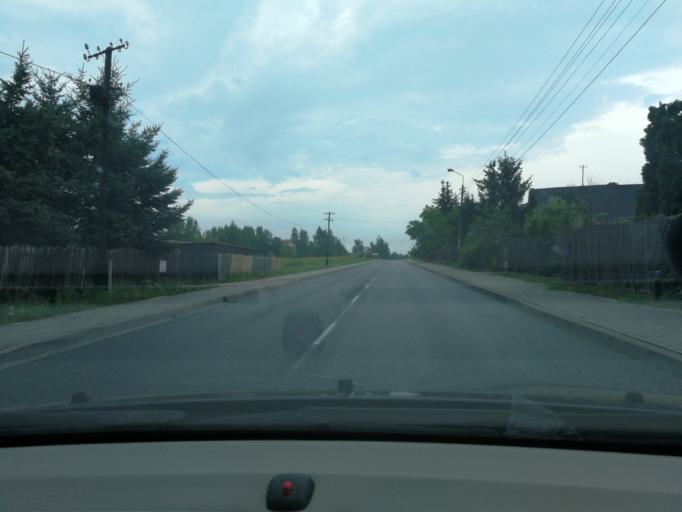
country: PL
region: Masovian Voivodeship
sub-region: Powiat zyrardowski
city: Radziejowice
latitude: 52.0061
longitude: 20.5565
